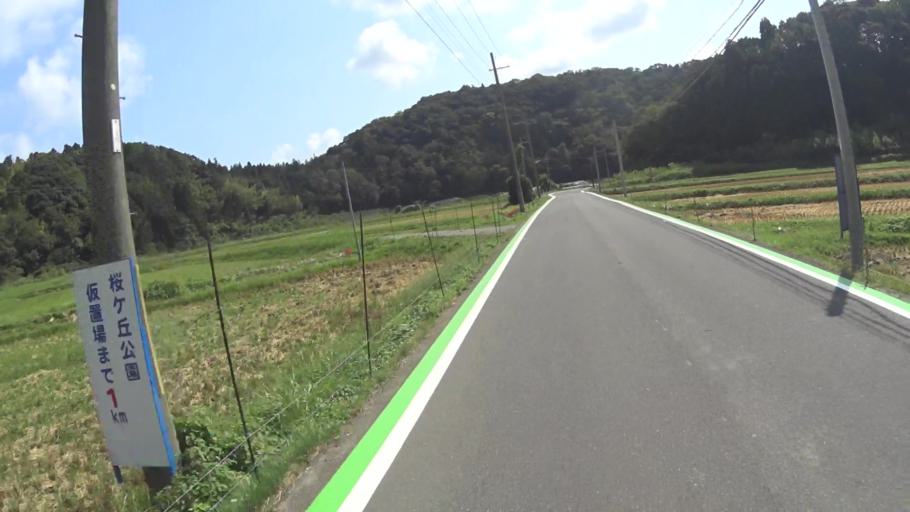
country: JP
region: Kyoto
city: Miyazu
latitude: 35.7166
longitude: 135.2521
